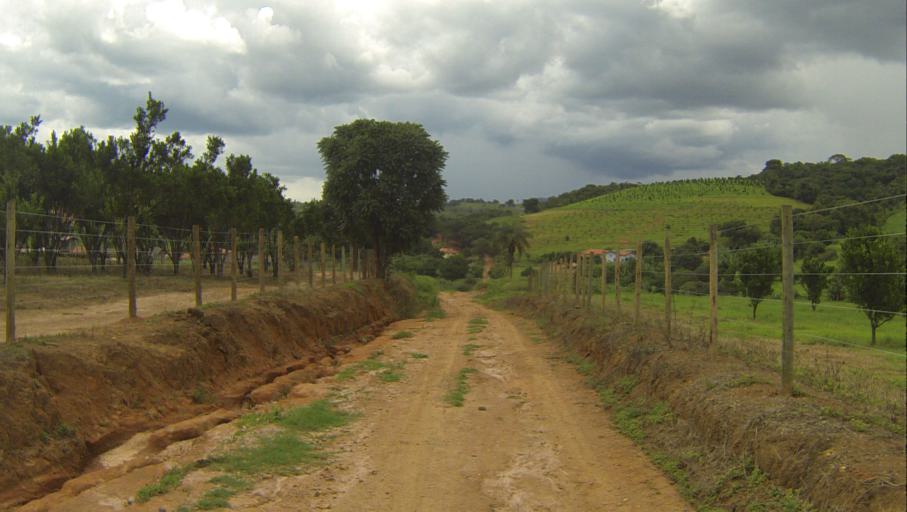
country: BR
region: Minas Gerais
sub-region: Brumadinho
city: Brumadinho
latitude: -20.1542
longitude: -44.1245
